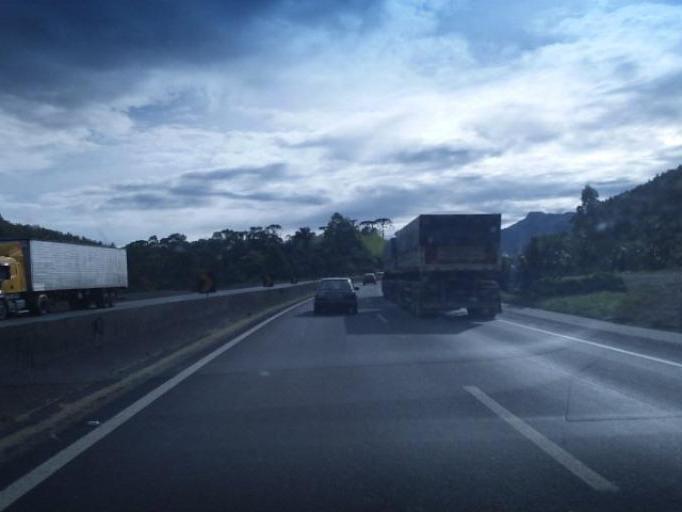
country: BR
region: Parana
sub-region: Antonina
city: Antonina
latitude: -25.1067
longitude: -48.7410
